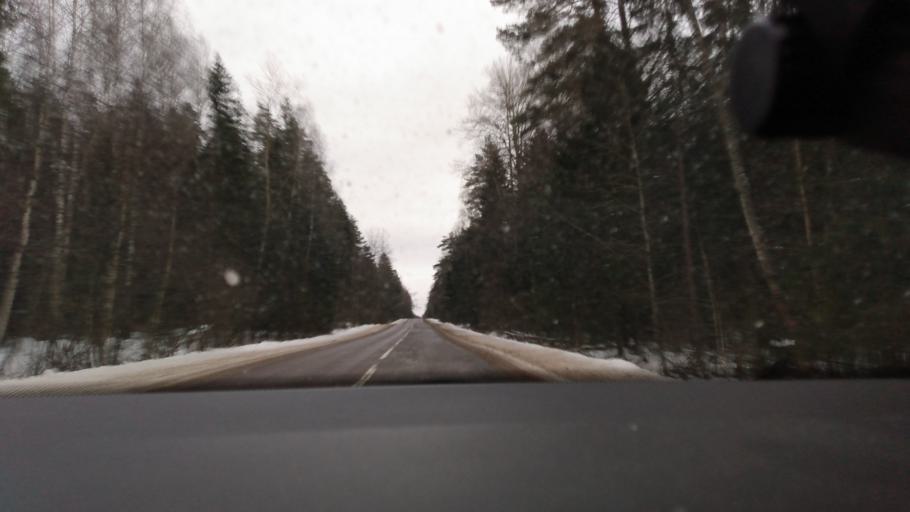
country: RU
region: Moskovskaya
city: Yegor'yevsk
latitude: 55.2183
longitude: 39.0824
